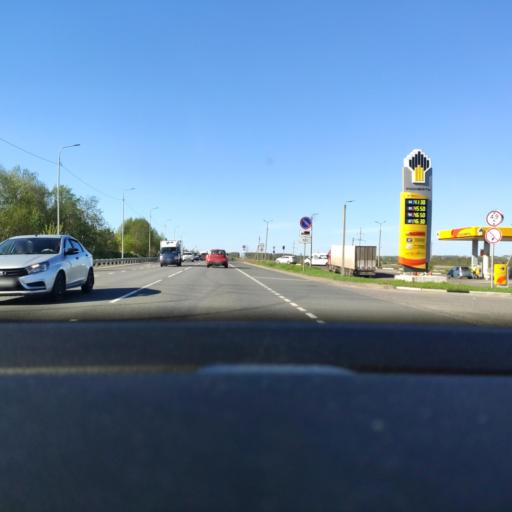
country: RU
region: Moskovskaya
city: Yakhroma
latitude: 56.3360
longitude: 37.4822
